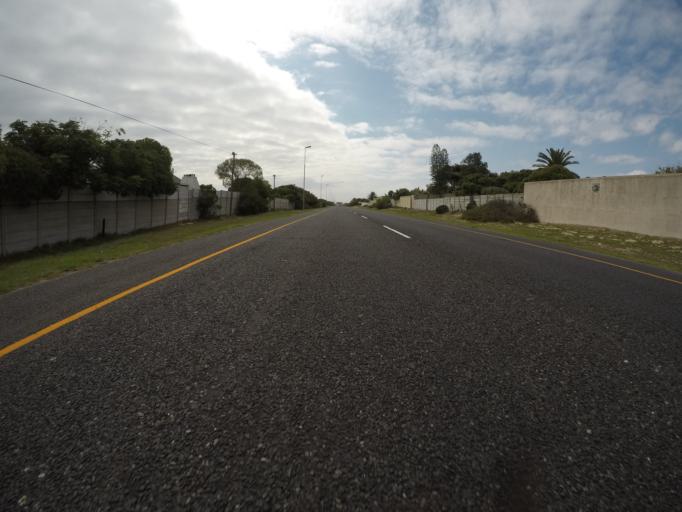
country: ZA
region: Western Cape
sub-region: City of Cape Town
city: Sunset Beach
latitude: -33.7221
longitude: 18.4471
